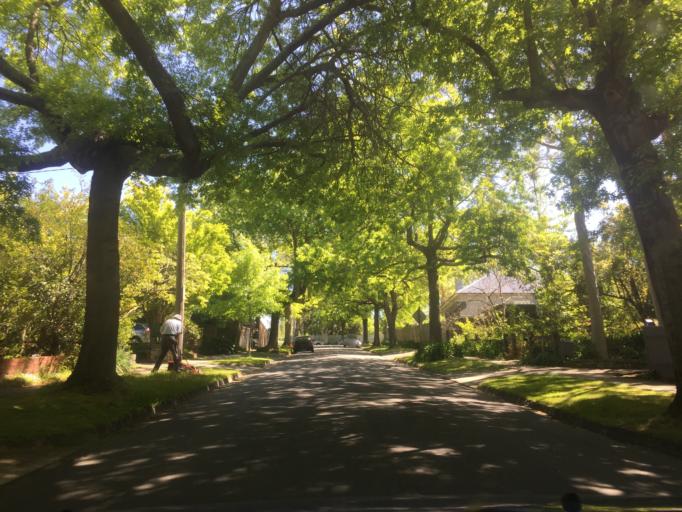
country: AU
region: Victoria
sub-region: Boroondara
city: Canterbury
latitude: -37.8200
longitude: 145.0832
